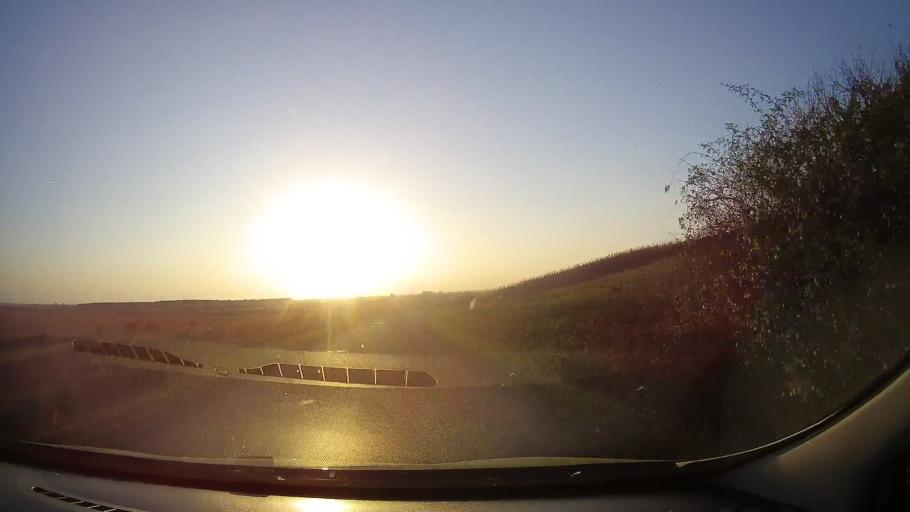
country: RO
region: Bihor
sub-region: Comuna Salard
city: Salard
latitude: 47.2490
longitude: 22.0188
